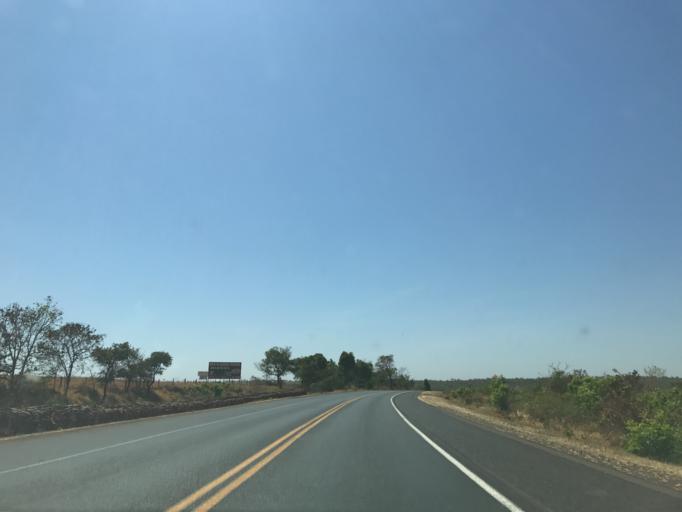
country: BR
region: Minas Gerais
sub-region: Prata
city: Prata
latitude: -19.3621
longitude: -48.9000
